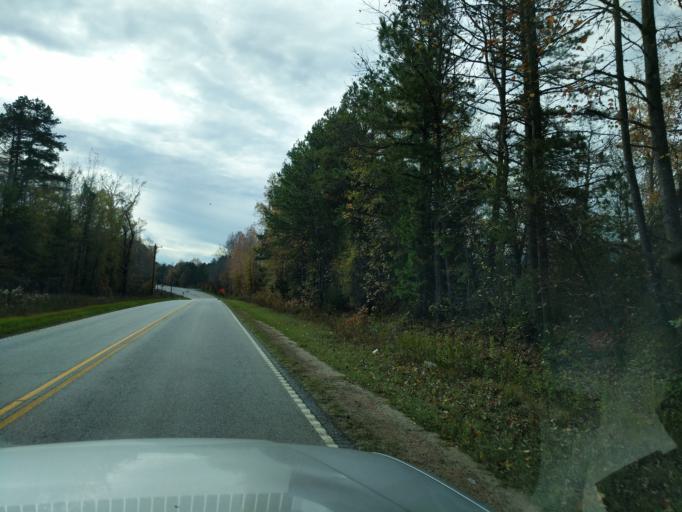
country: US
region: South Carolina
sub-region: Laurens County
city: Watts Mills
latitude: 34.5648
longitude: -82.0061
